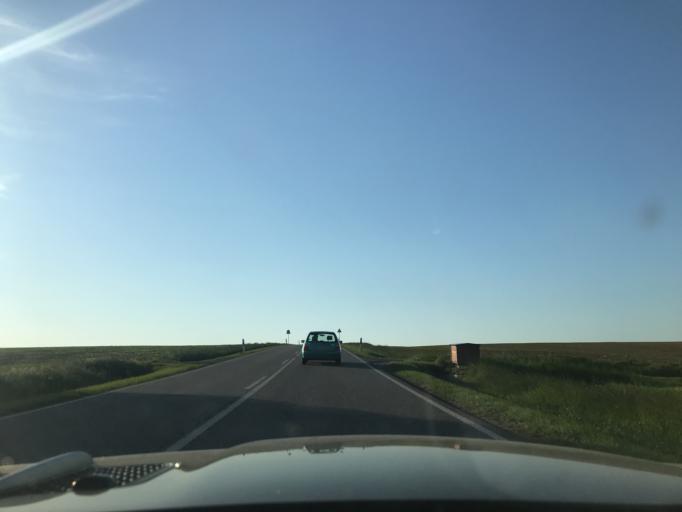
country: DE
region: Thuringia
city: Bad Langensalza
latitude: 51.0607
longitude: 10.6480
